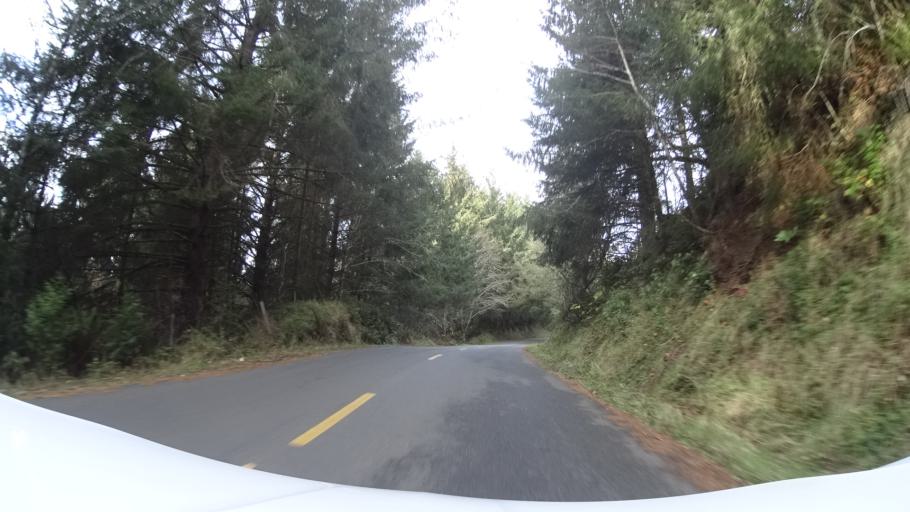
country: US
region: California
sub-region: Humboldt County
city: Ferndale
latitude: 40.5475
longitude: -124.2756
